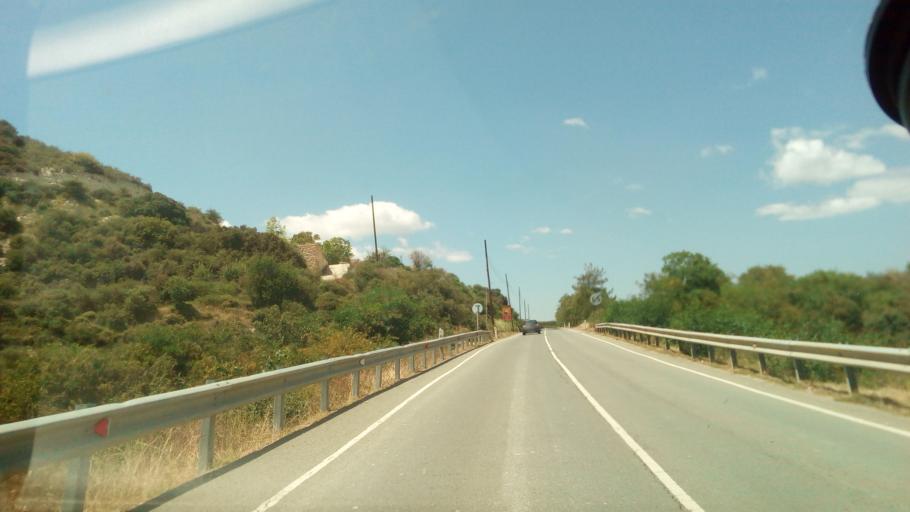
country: CY
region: Limassol
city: Pachna
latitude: 34.7690
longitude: 32.8364
